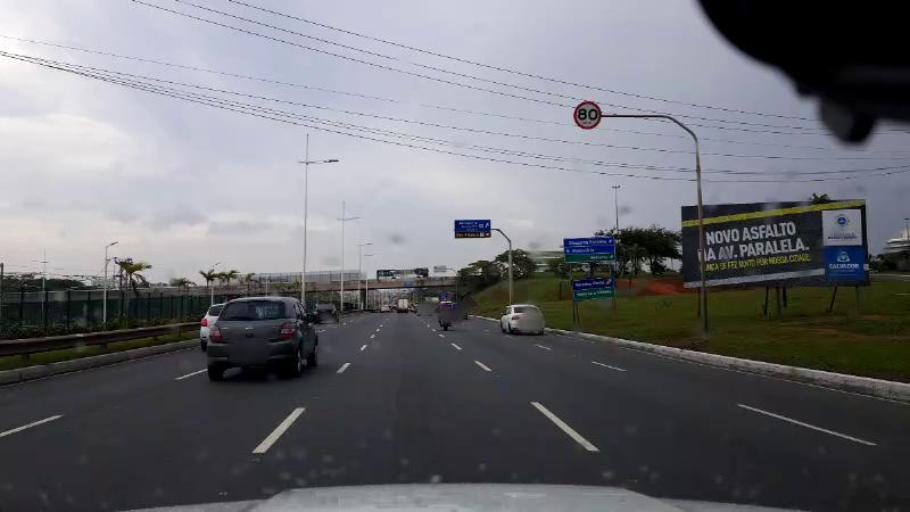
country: BR
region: Bahia
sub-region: Salvador
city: Salvador
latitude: -12.9482
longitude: -38.4239
